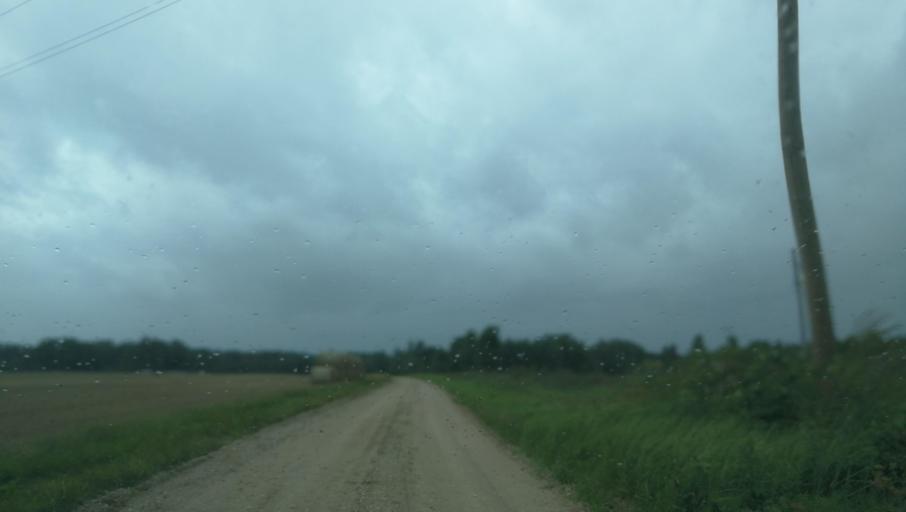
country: LV
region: Beverina
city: Murmuiza
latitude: 57.4079
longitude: 25.4576
